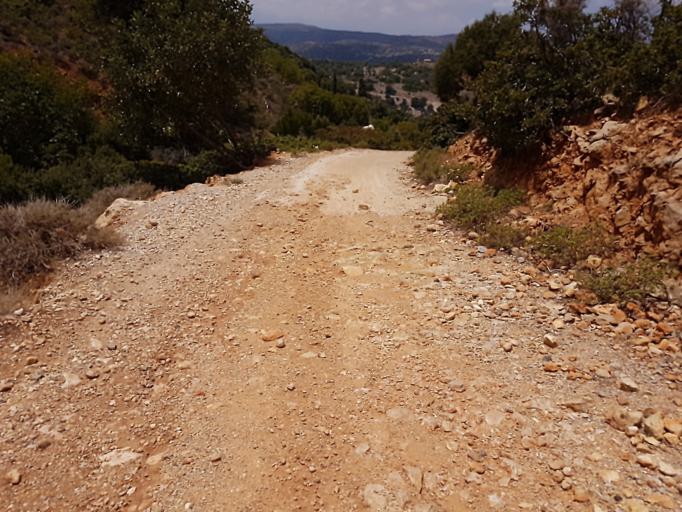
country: GR
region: Crete
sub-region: Nomos Irakleiou
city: Limin Khersonisou
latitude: 35.2943
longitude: 25.3786
